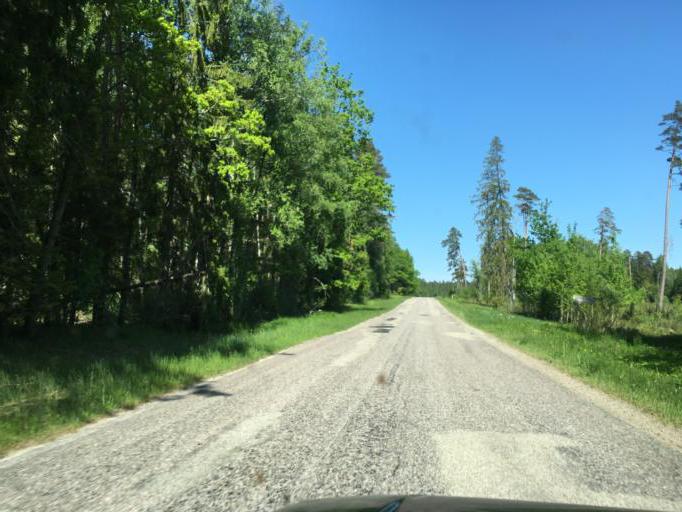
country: LV
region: Dundaga
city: Dundaga
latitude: 57.4775
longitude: 22.3269
